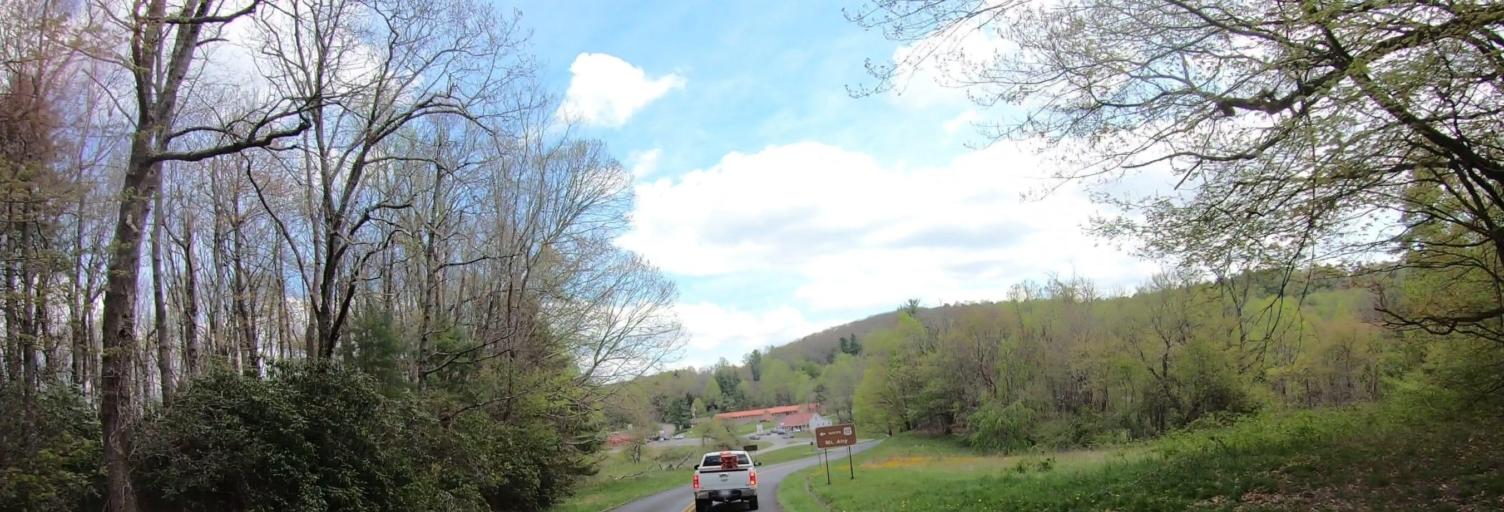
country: US
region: Virginia
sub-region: Carroll County
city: Cana
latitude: 36.6653
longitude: -80.6942
